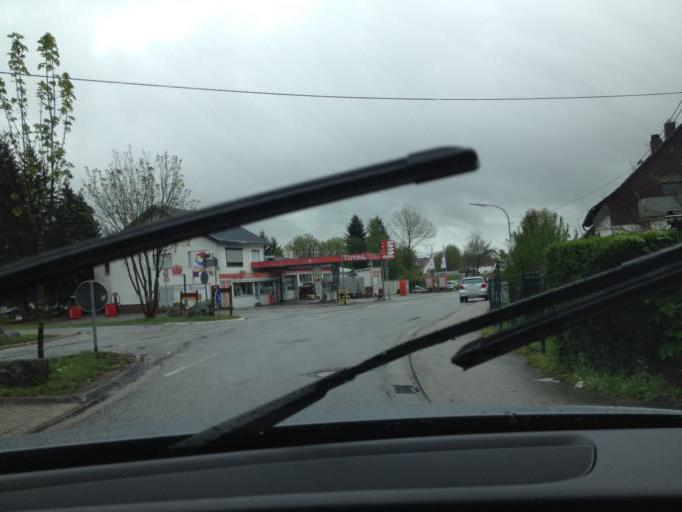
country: DE
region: Rheinland-Pfalz
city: Reichweiler
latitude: 49.5252
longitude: 7.2623
